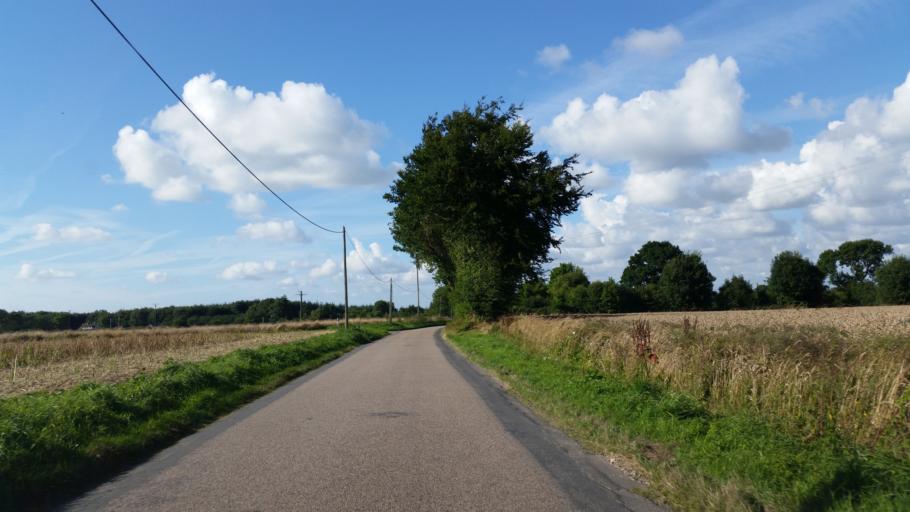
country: FR
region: Lower Normandy
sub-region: Departement du Calvados
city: Equemauville
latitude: 49.3845
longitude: 0.2266
